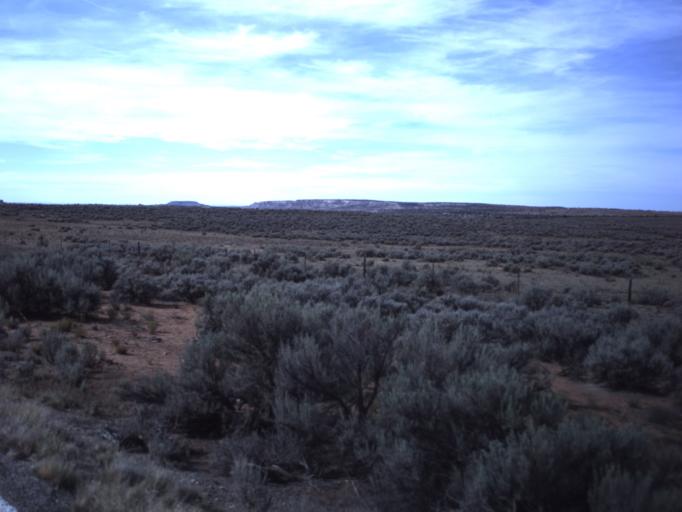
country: US
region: Utah
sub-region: San Juan County
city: Blanding
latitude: 37.4153
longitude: -109.3346
